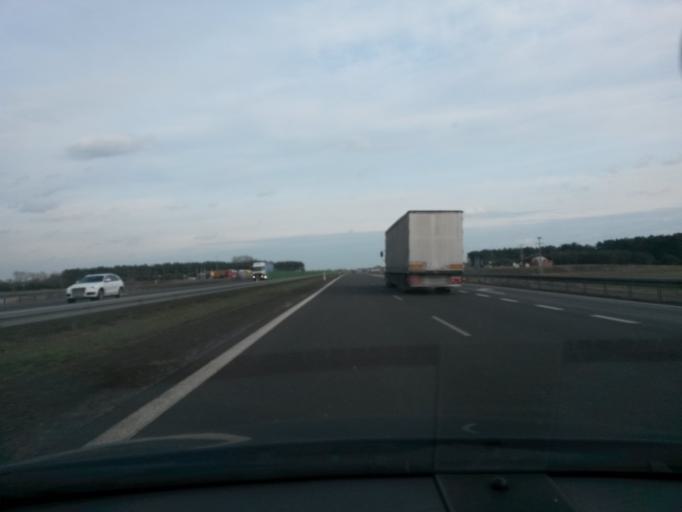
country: PL
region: Greater Poland Voivodeship
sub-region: Powiat kolski
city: Dabie
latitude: 52.0987
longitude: 18.7682
